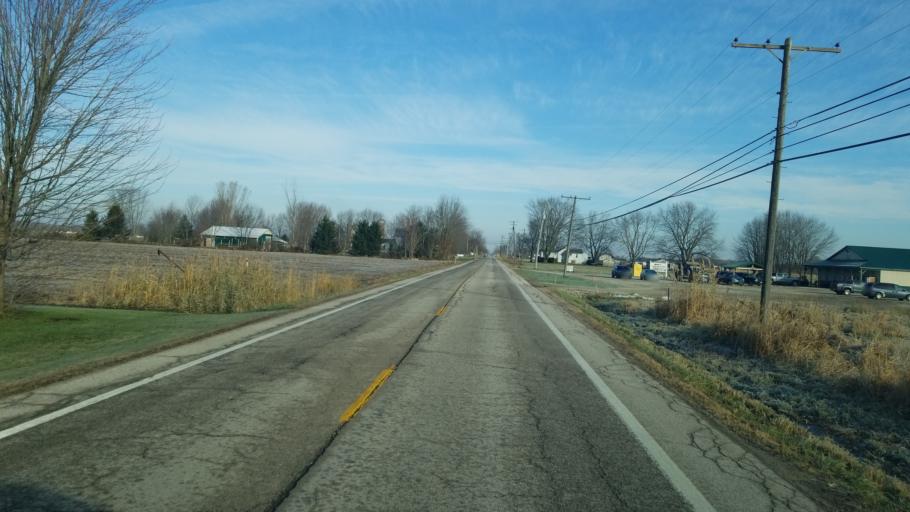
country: US
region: Ohio
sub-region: Ashtabula County
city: Jefferson
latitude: 41.7400
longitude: -80.6674
